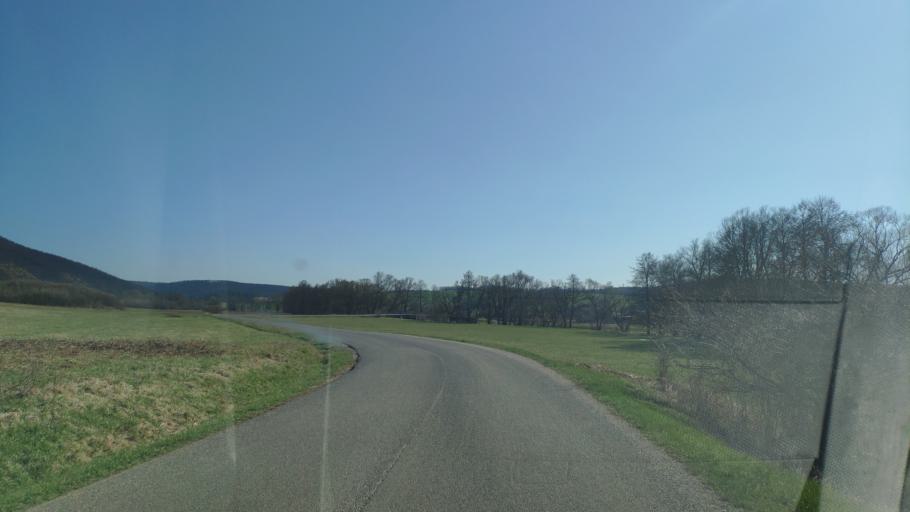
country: SK
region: Banskobystricky
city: Revuca
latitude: 48.5416
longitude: 20.3031
